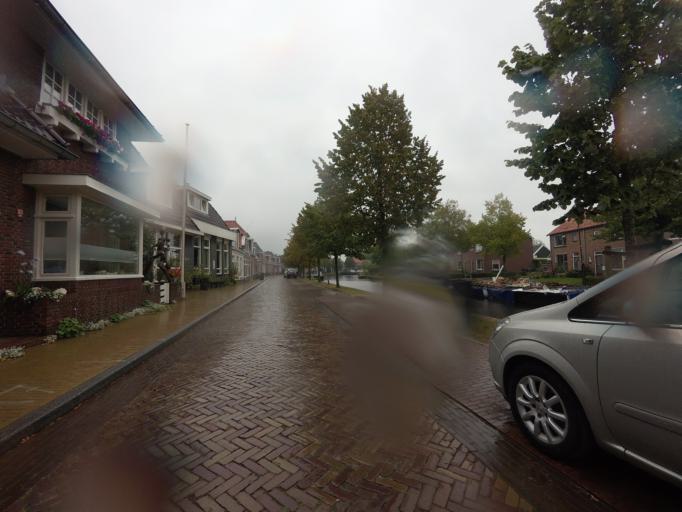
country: NL
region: Friesland
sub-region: Gemeente Boarnsterhim
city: Aldeboarn
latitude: 53.0484
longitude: 5.8949
